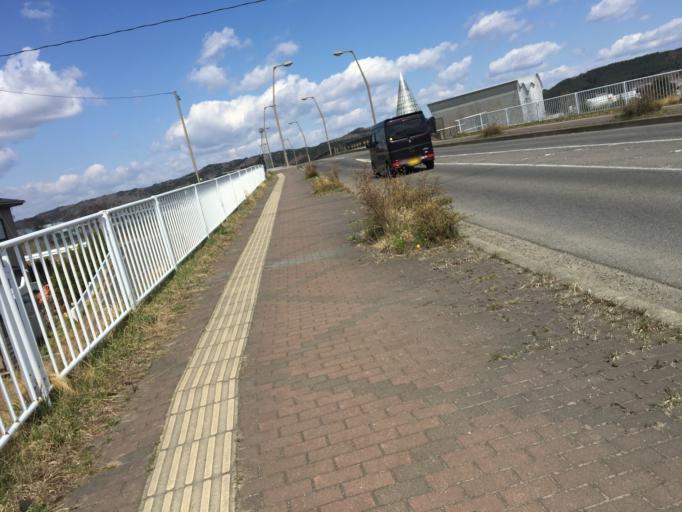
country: JP
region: Aomori
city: Hachinohe
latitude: 40.1892
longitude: 141.7799
